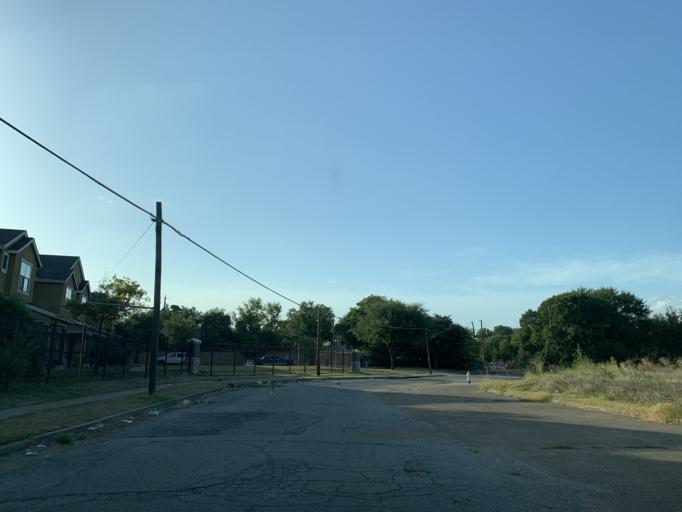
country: US
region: Texas
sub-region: Dallas County
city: Dallas
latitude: 32.7572
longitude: -96.7448
